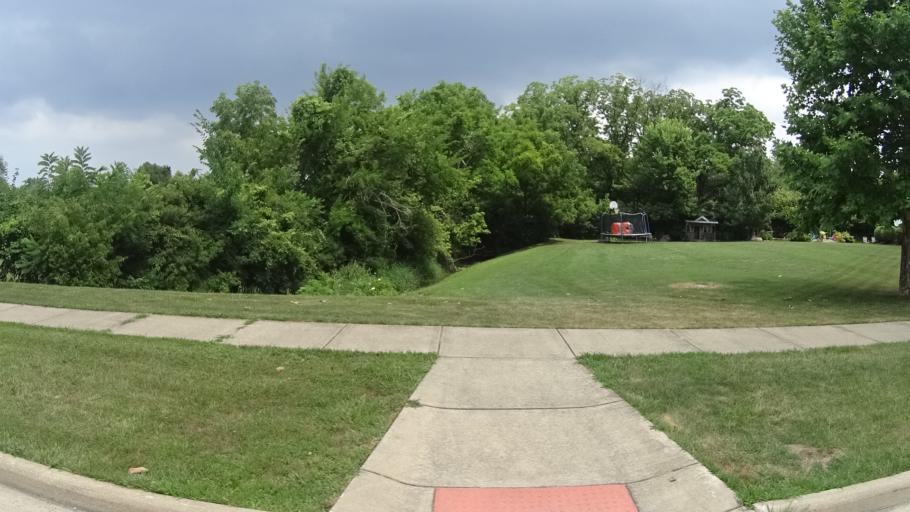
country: US
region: Ohio
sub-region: Erie County
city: Sandusky
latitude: 41.4383
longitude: -82.7599
